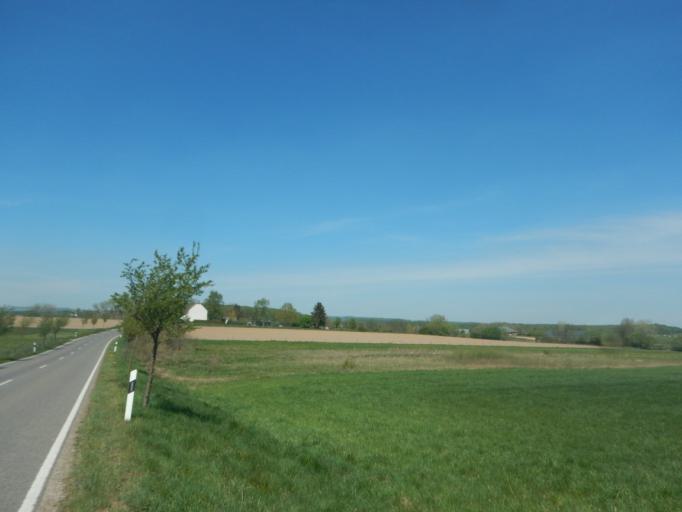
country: LU
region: Diekirch
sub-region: Canton de Redange
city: Redange-sur-Attert
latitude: 49.7489
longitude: 5.9146
